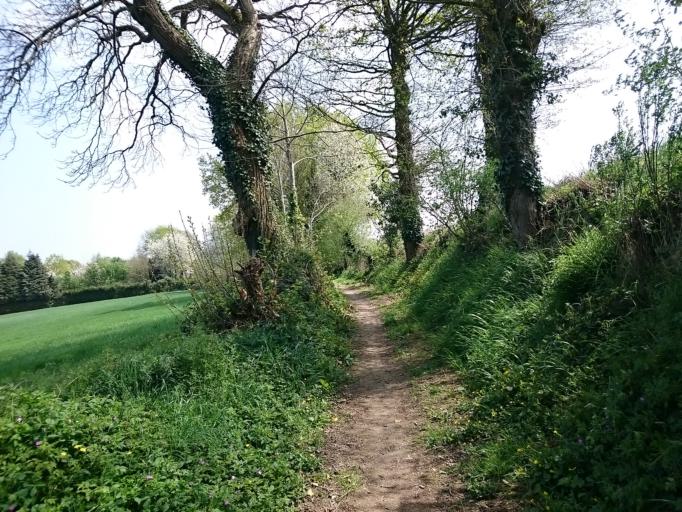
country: FR
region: Brittany
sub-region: Departement d'Ille-et-Vilaine
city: Chanteloup
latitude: 47.9341
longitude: -1.6062
